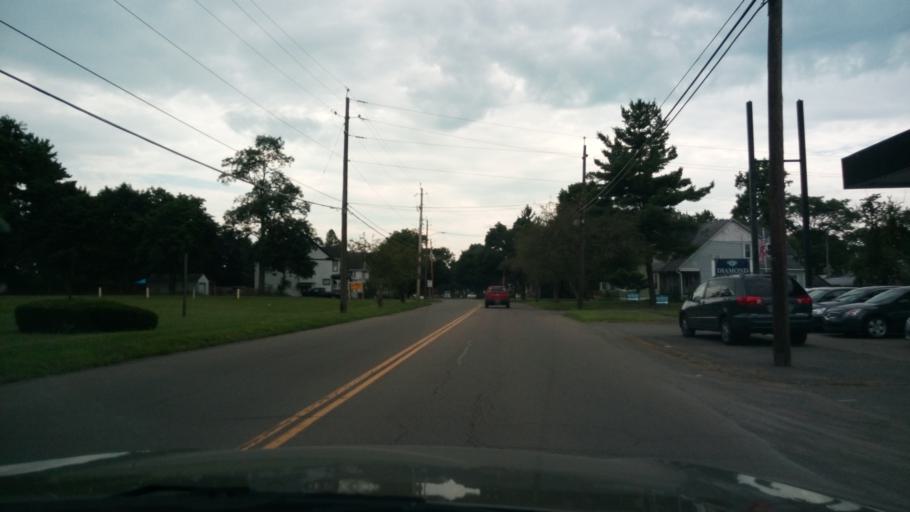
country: US
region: New York
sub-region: Chemung County
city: Elmira Heights
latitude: 42.1154
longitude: -76.8082
